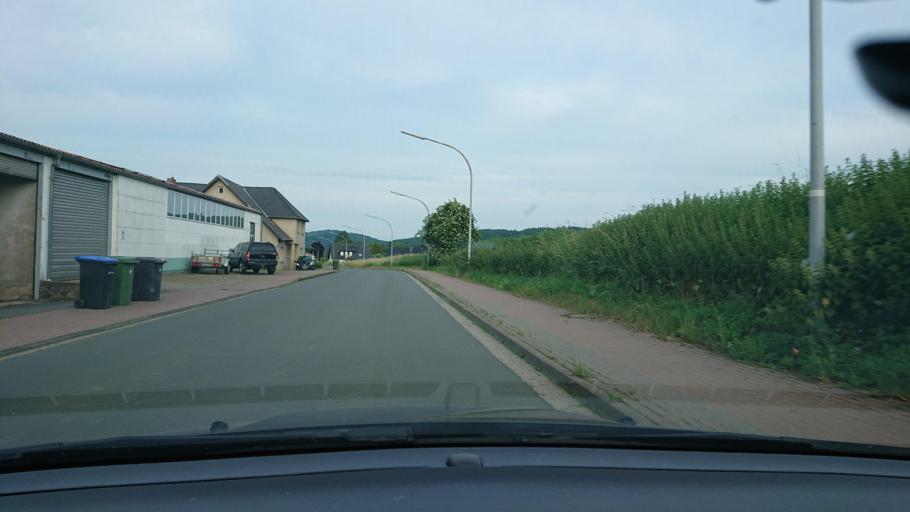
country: DE
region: North Rhine-Westphalia
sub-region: Regierungsbezirk Detmold
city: Rodinghausen
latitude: 52.2789
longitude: 8.4794
